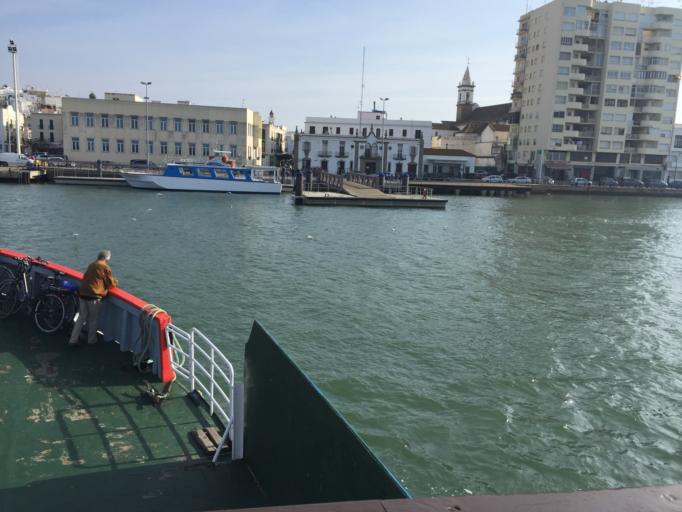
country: ES
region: Andalusia
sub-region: Provincia de Huelva
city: Ayamonte
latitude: 37.2142
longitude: -7.4111
